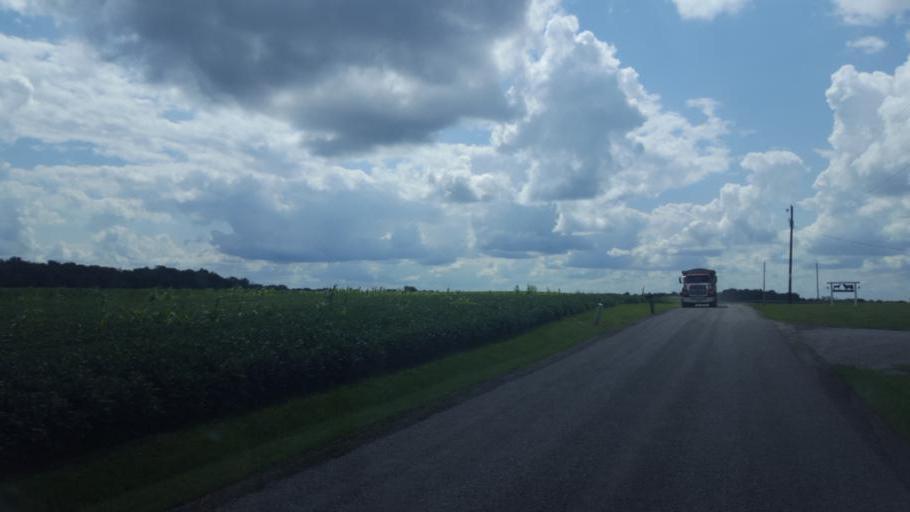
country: US
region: Ohio
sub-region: Morrow County
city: Mount Gilead
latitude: 40.5525
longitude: -82.7153
